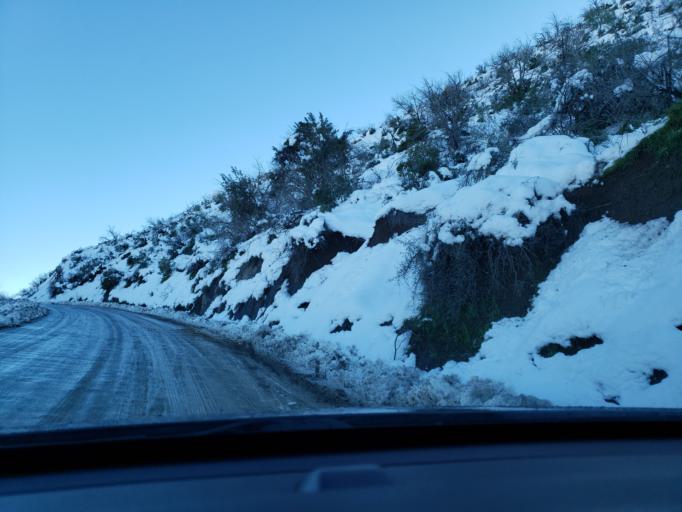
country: US
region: Arizona
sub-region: Maricopa County
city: Carefree
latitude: 33.9015
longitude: -111.8257
